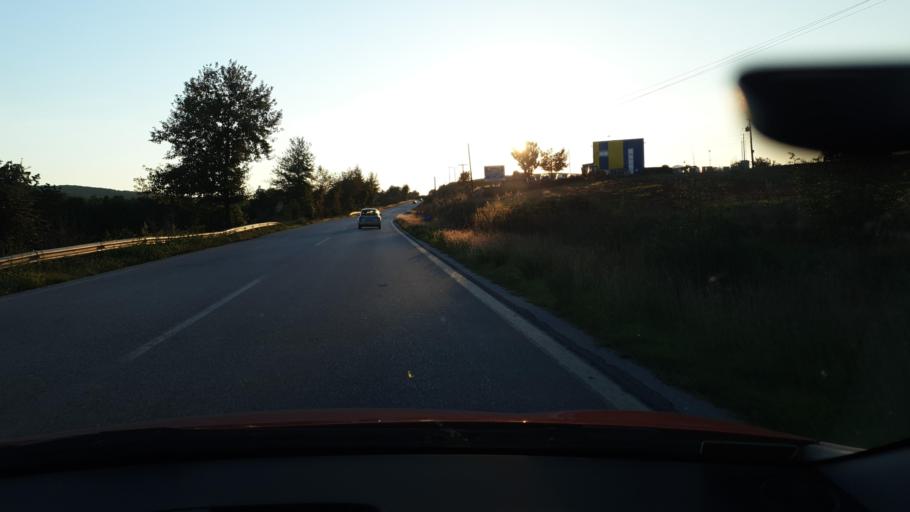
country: GR
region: Central Macedonia
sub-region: Nomos Chalkidikis
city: Galatista
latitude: 40.4649
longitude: 23.3622
